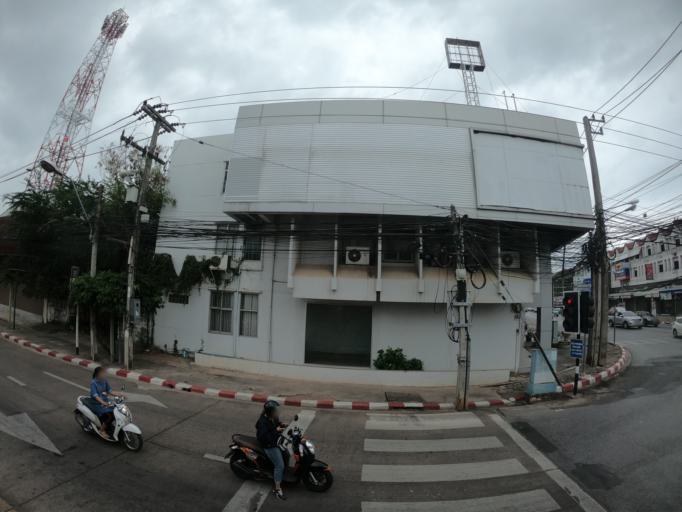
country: TH
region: Roi Et
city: Roi Et
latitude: 16.0543
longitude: 103.6416
